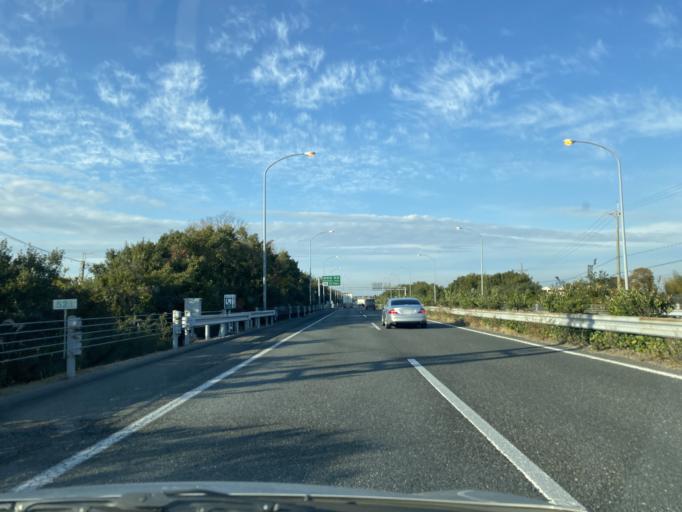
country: JP
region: Osaka
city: Izumi
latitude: 34.4296
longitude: 135.4470
